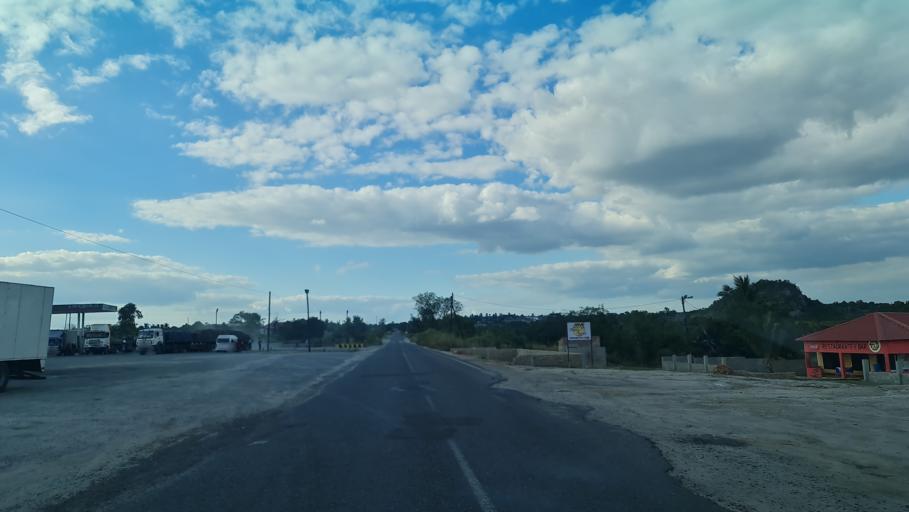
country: MZ
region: Manica
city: Chimoio
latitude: -19.2194
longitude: 33.9218
